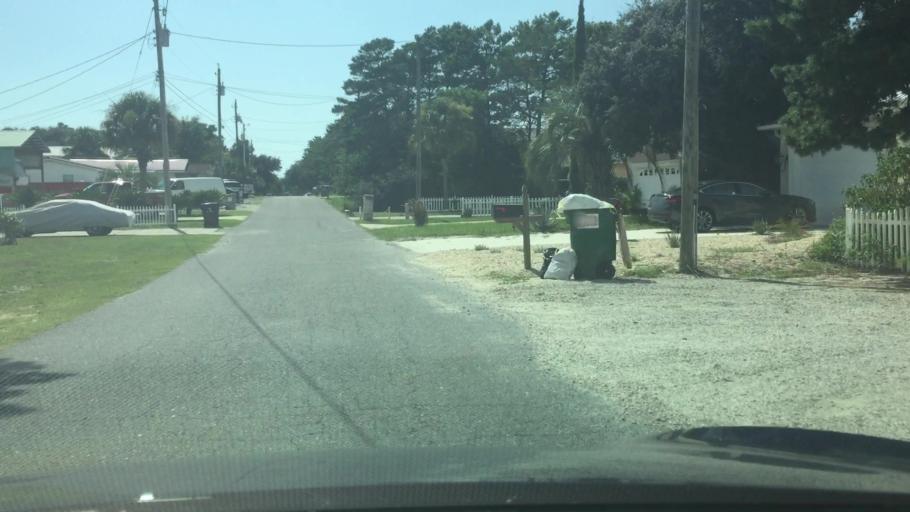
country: US
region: Florida
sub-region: Bay County
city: Laguna Beach
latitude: 30.2589
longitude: -85.9541
